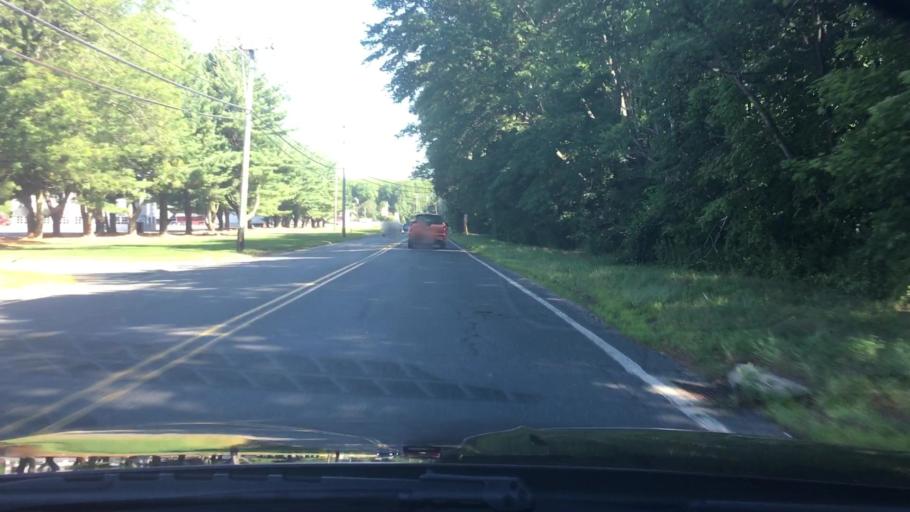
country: US
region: Massachusetts
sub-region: Hampden County
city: East Longmeadow
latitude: 42.0445
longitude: -72.5184
